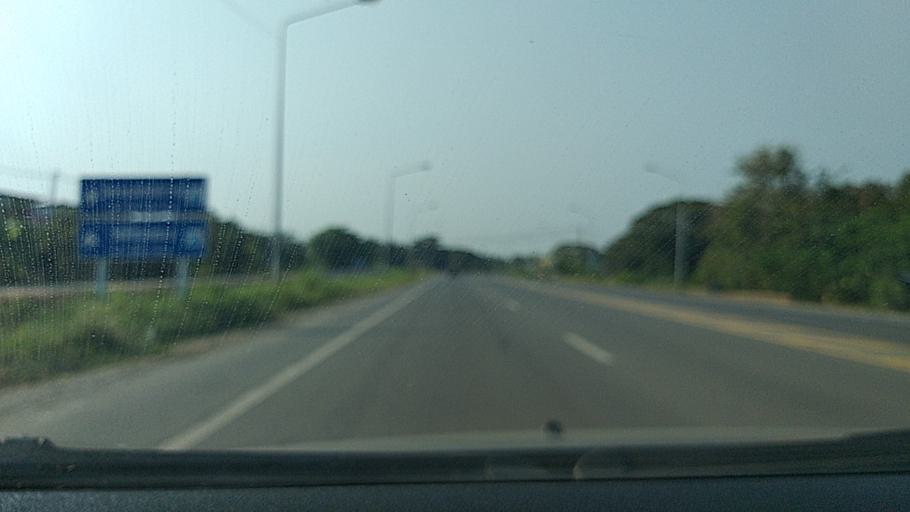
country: TH
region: Sing Buri
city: Sing Buri
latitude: 14.8598
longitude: 100.4075
